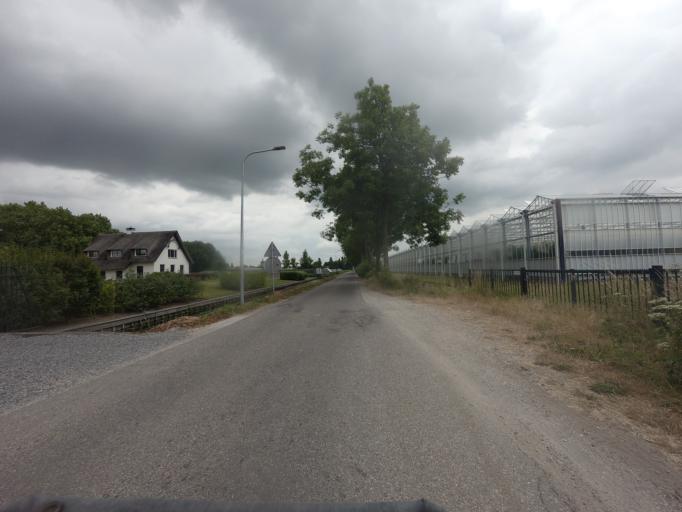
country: NL
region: Utrecht
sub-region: Stichtse Vecht
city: Spechtenkamp
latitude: 52.0954
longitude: 4.9883
